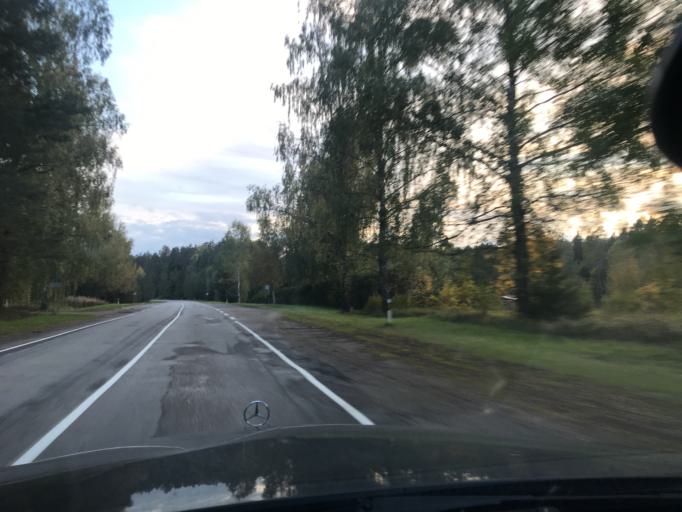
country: EE
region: Valgamaa
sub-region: Torva linn
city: Torva
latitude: 58.0052
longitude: 26.0832
